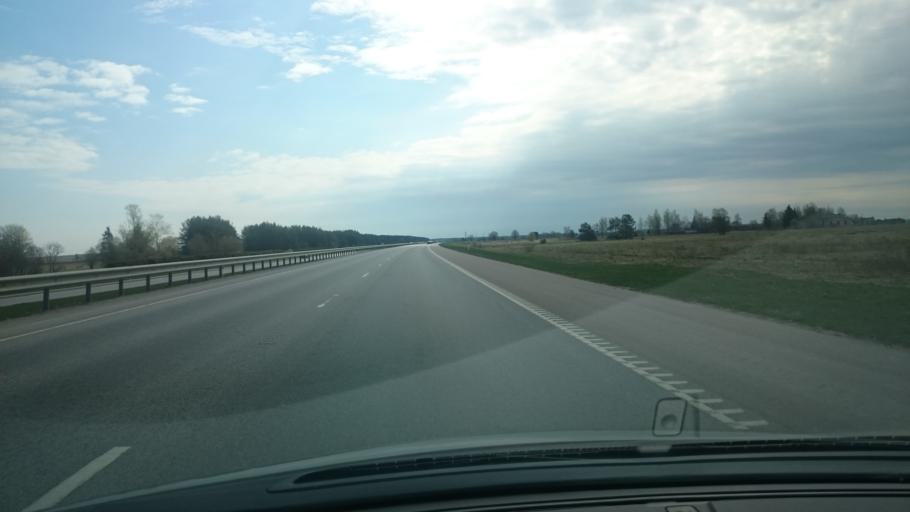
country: EE
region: Harju
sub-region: Maardu linn
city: Maardu
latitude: 59.4492
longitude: 25.0785
